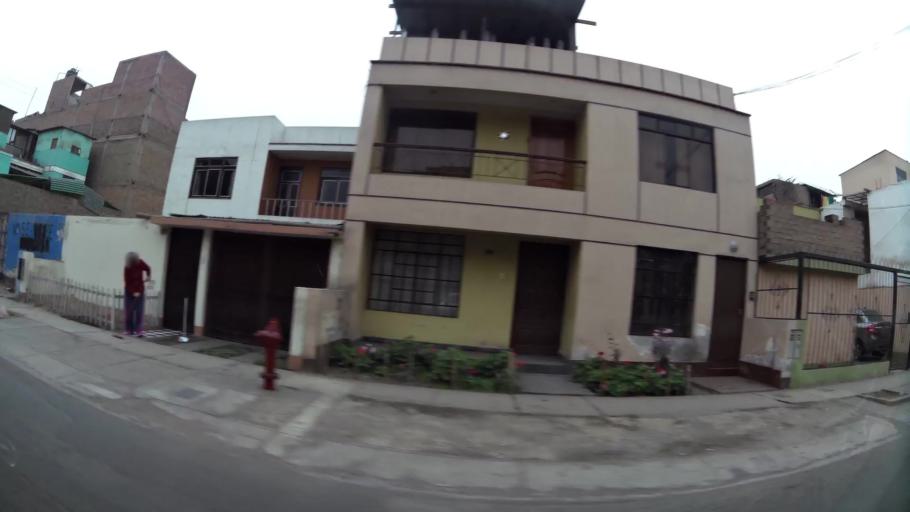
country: PE
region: Lima
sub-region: Lima
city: Surco
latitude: -12.1689
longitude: -76.9766
